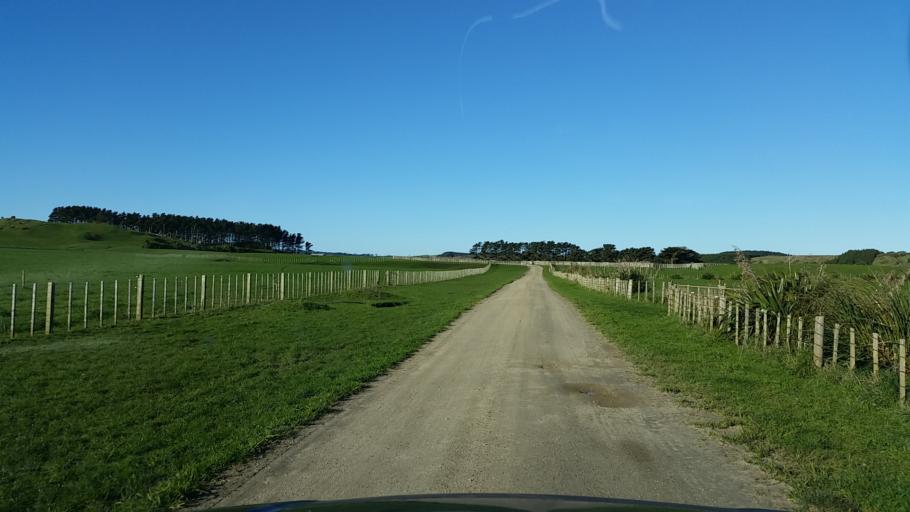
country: NZ
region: Taranaki
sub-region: South Taranaki District
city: Patea
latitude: -39.8375
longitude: 174.6967
